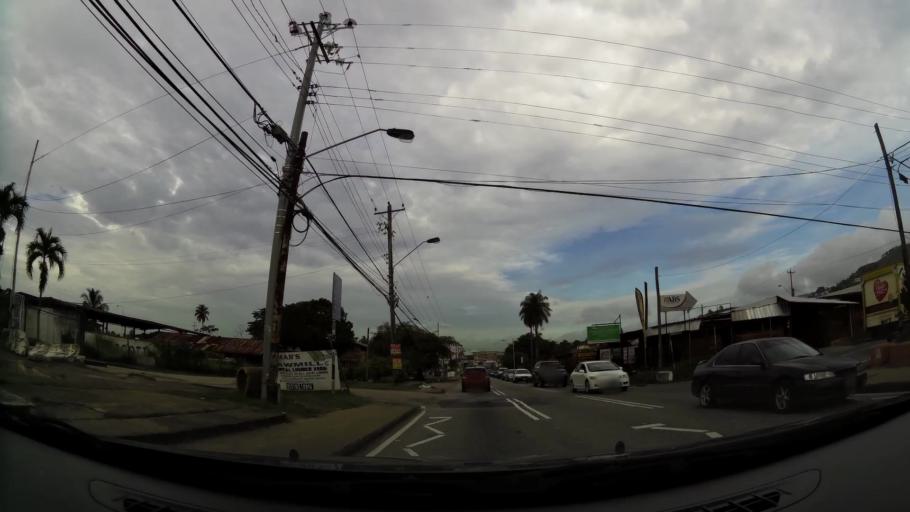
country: TT
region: Tunapuna/Piarco
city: Tunapuna
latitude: 10.6502
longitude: -61.4344
